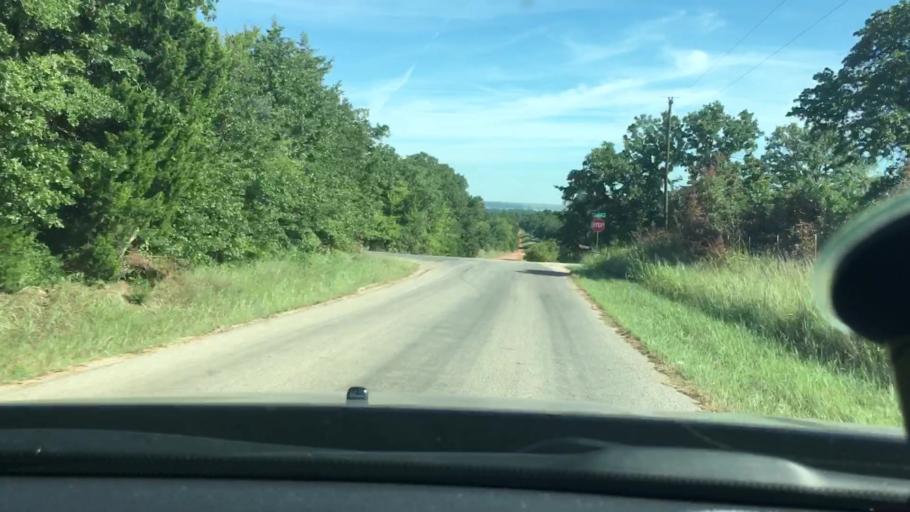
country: US
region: Oklahoma
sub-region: Carter County
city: Lone Grove
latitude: 34.2668
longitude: -97.2474
